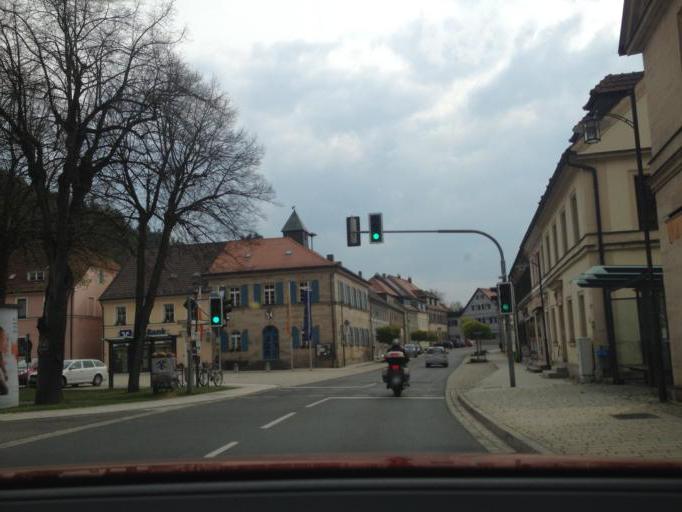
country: DE
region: Bavaria
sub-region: Upper Franconia
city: Goldkronach
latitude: 50.0117
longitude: 11.6874
